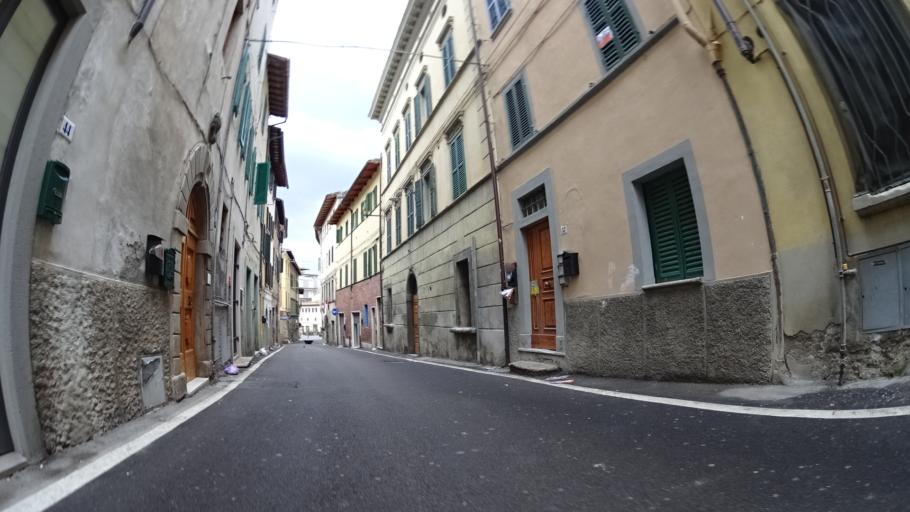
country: IT
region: Tuscany
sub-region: Provincia di Siena
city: Poggibonsi
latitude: 43.4676
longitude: 11.1452
